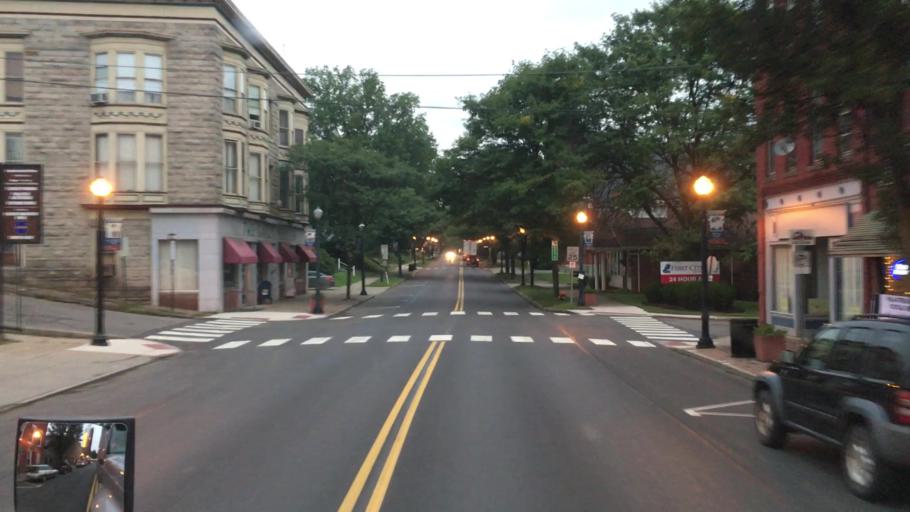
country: US
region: Pennsylvania
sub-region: Bradford County
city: Towanda
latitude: 41.7681
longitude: -76.4431
